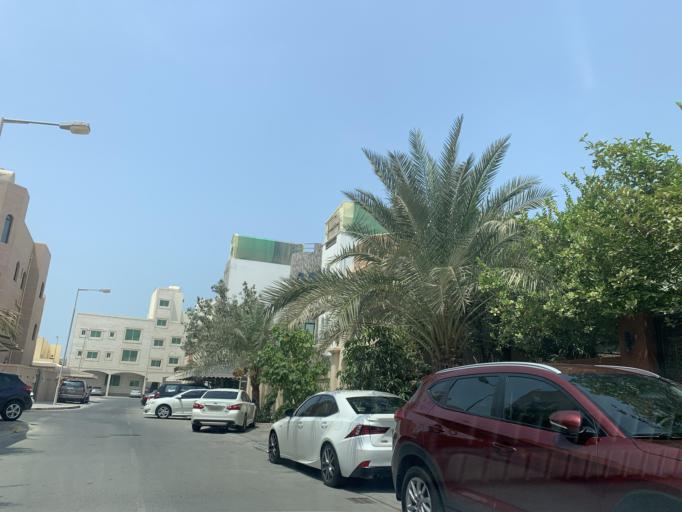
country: BH
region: Muharraq
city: Al Hadd
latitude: 26.2764
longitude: 50.6517
